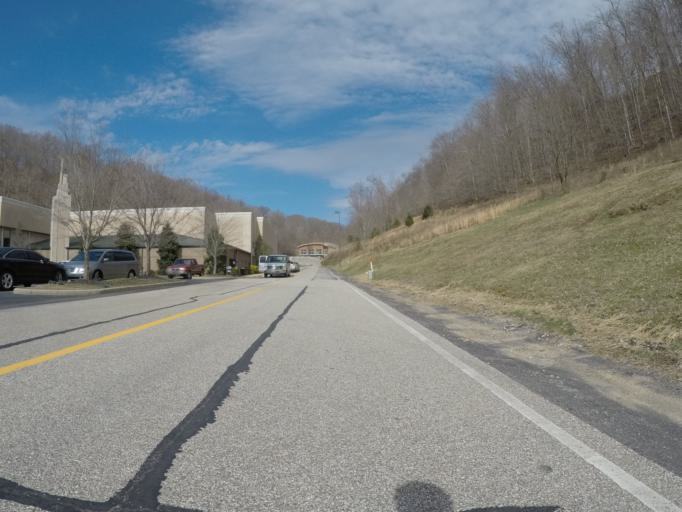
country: US
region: West Virginia
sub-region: Cabell County
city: Huntington
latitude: 38.3978
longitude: -82.4567
